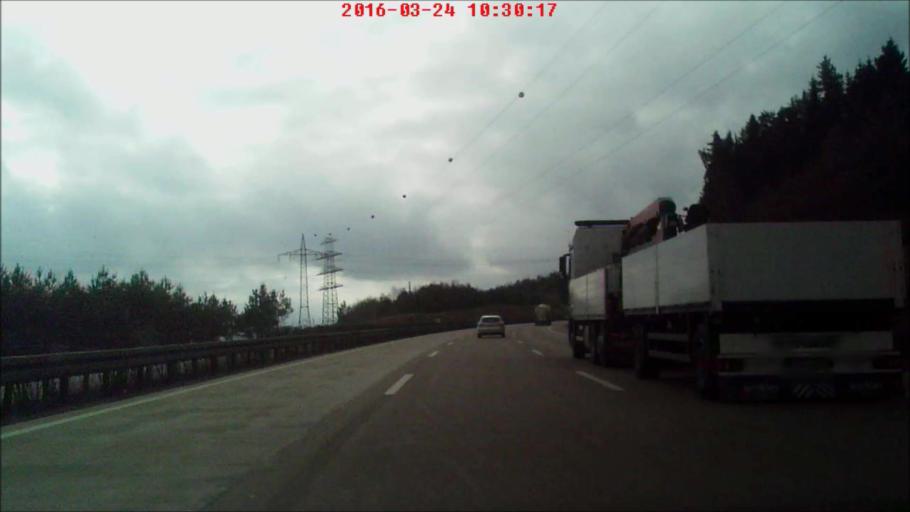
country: DE
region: Thuringia
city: Behringen
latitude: 50.7635
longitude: 11.0034
